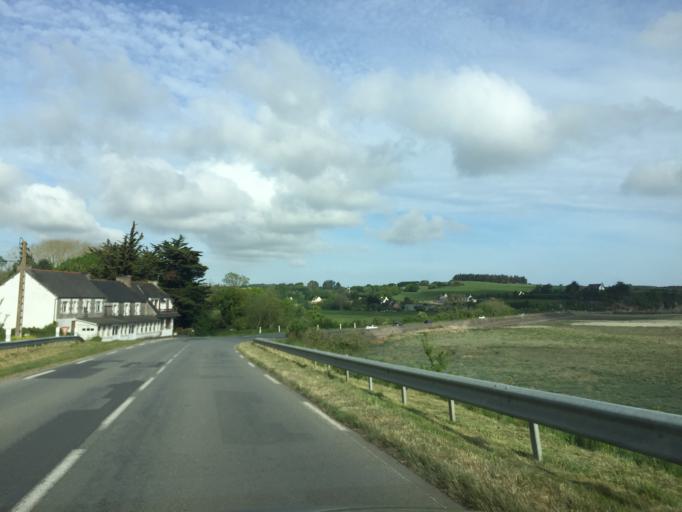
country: FR
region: Brittany
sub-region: Departement des Cotes-d'Armor
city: Matignon
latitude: 48.6098
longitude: -2.3151
